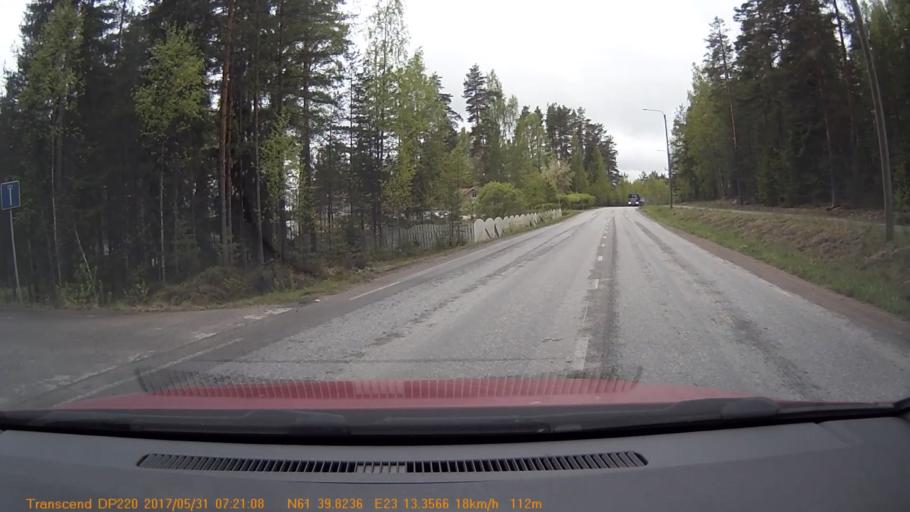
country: FI
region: Pirkanmaa
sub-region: Tampere
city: Haemeenkyroe
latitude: 61.6637
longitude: 23.2227
